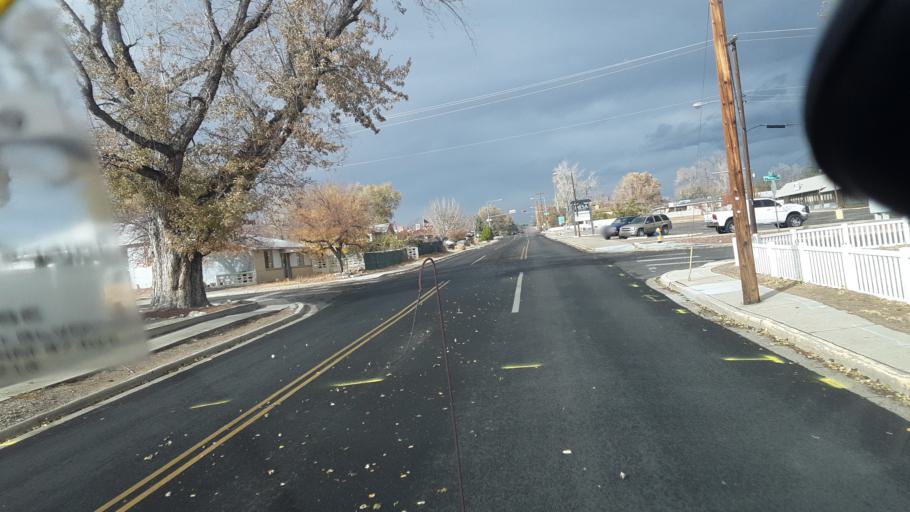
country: US
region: New Mexico
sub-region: San Juan County
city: Farmington
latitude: 36.7394
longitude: -108.1979
